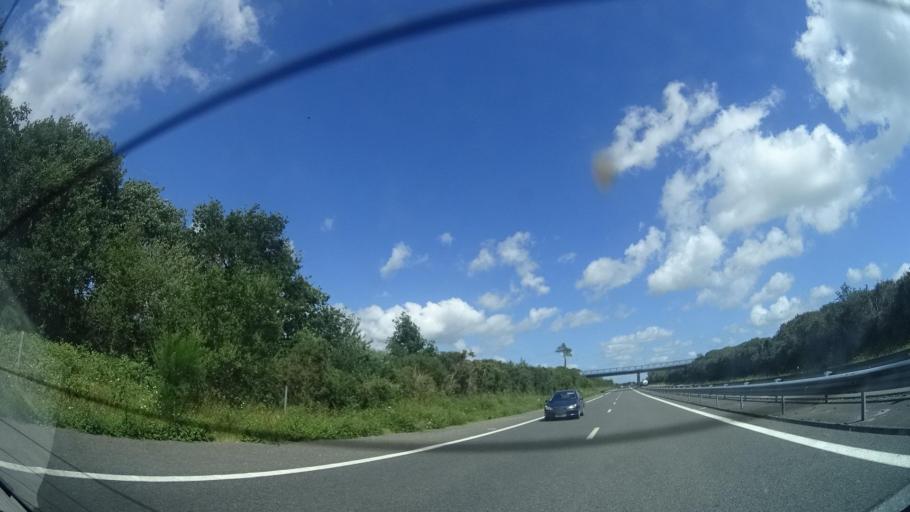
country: FR
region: Brittany
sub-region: Departement du Morbihan
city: Pluherlin
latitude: 47.6699
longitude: -2.3361
